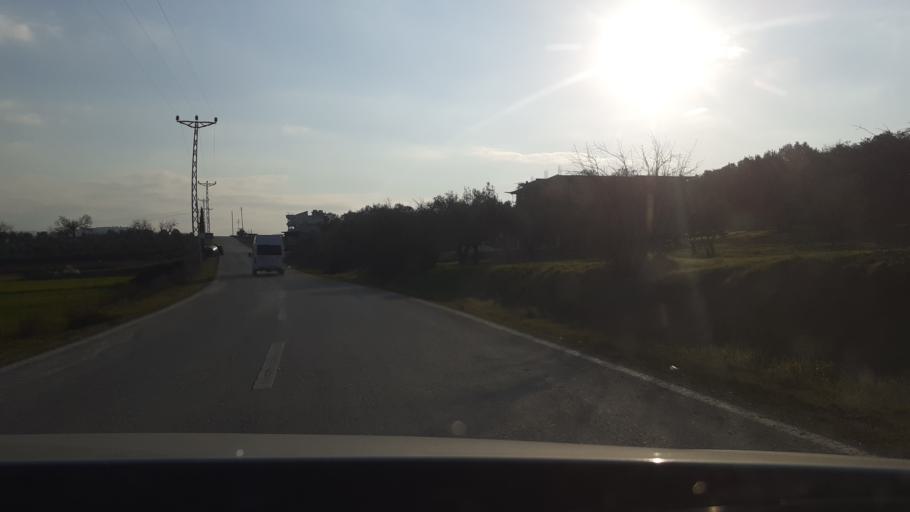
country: TR
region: Hatay
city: Boynuyogun
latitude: 36.1375
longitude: 36.3139
